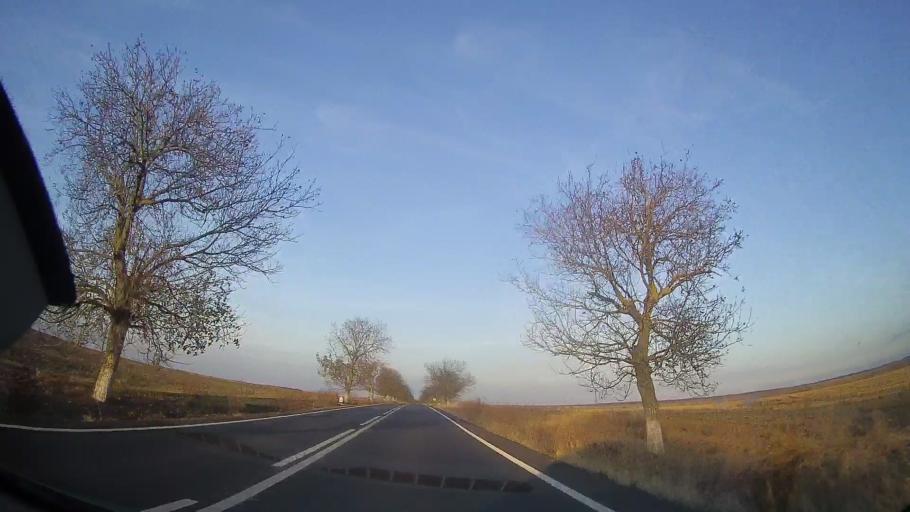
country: RO
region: Constanta
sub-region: Comuna Amzacea
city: Amzacea
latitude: 43.9380
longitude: 28.3679
